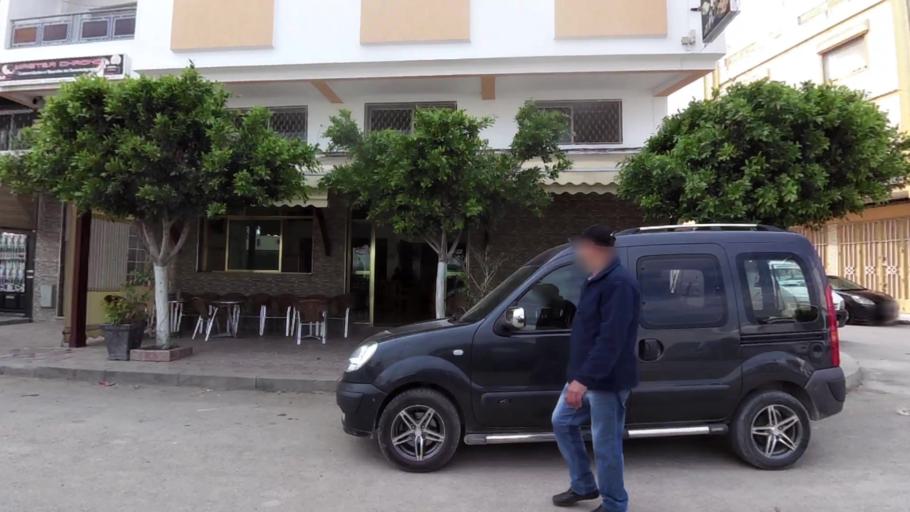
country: MA
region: Tanger-Tetouan
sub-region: Tanger-Assilah
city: Tangier
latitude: 35.7527
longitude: -5.7938
